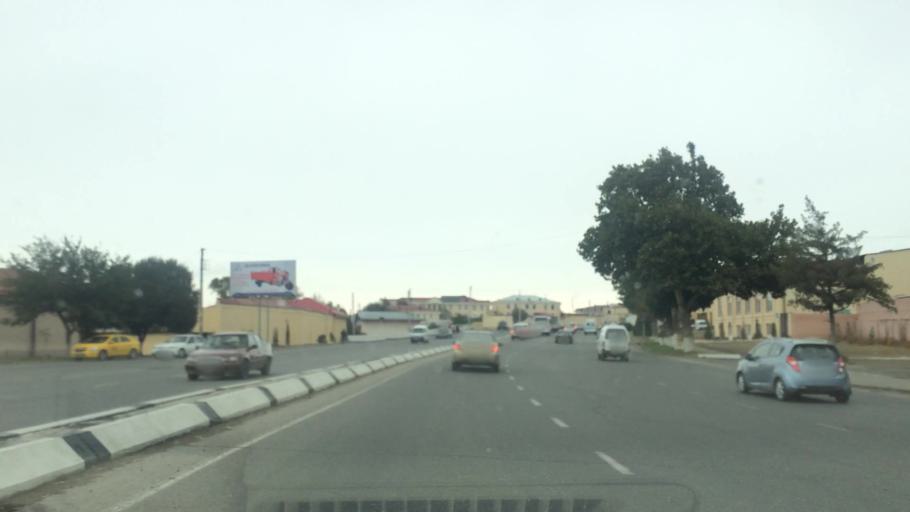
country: UZ
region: Samarqand
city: Samarqand
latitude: 39.6768
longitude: 67.0067
